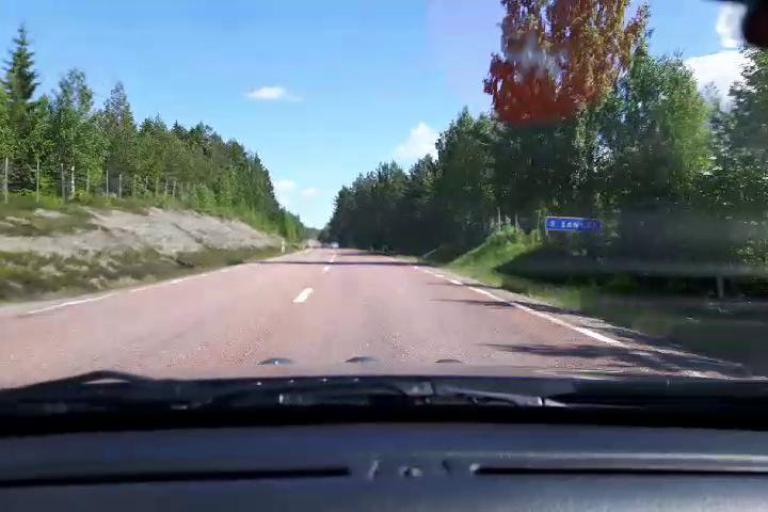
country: SE
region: Gaevleborg
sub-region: Hudiksvalls Kommun
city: Delsbo
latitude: 61.7710
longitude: 16.6867
